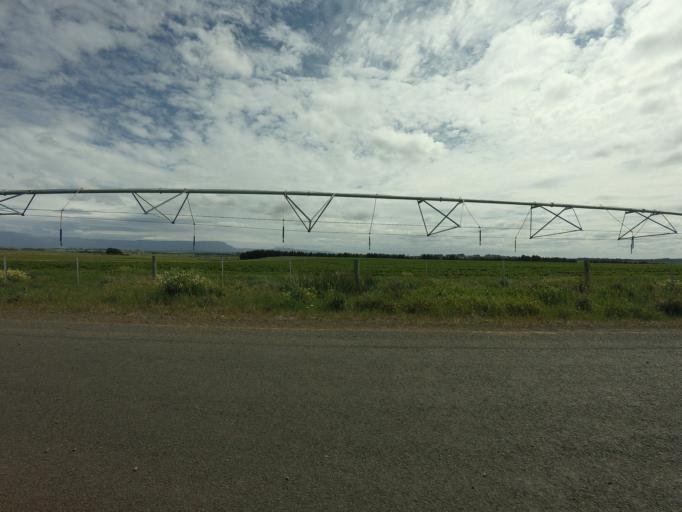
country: AU
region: Tasmania
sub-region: Northern Midlands
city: Longford
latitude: -41.6564
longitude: 147.1492
